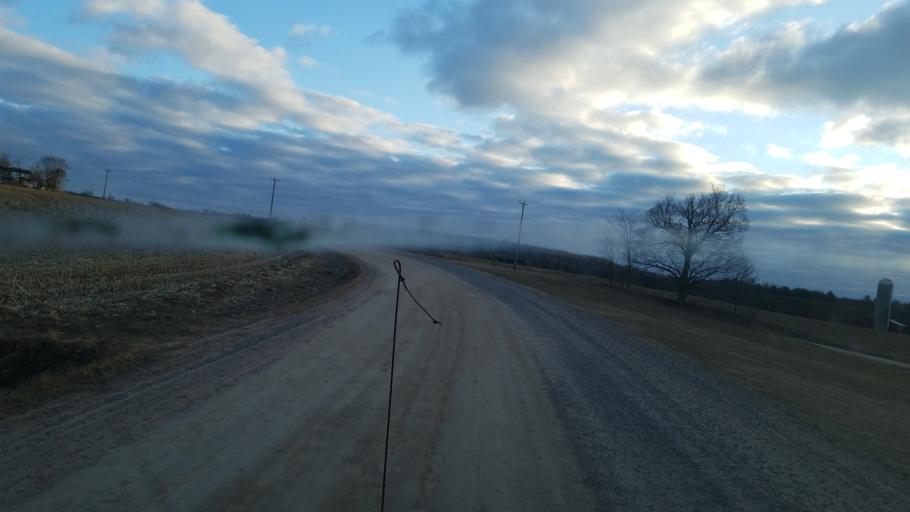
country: US
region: Wisconsin
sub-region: Clark County
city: Neillsville
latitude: 44.5967
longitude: -90.4576
